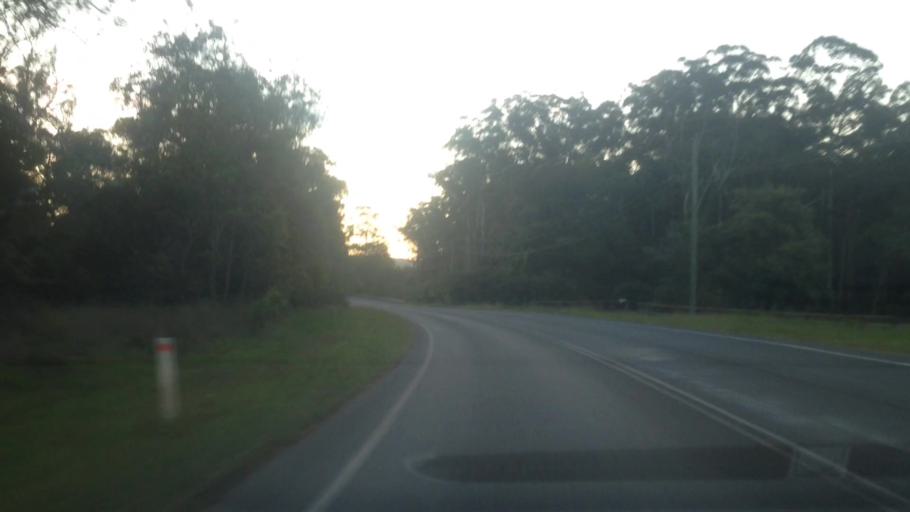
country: AU
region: New South Wales
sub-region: Lake Macquarie Shire
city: Cooranbong
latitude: -33.0713
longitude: 151.4735
